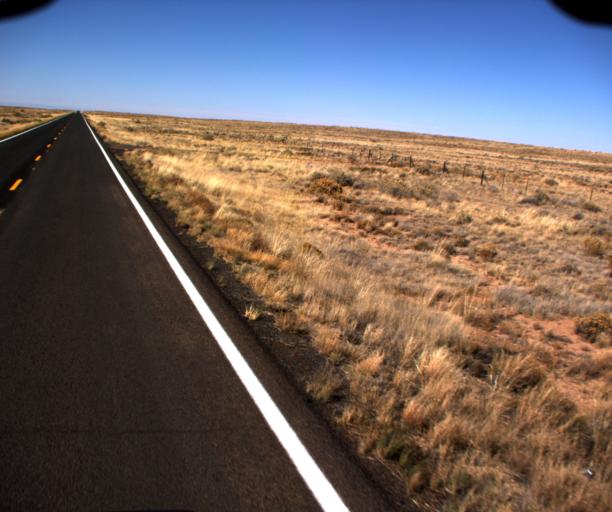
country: US
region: Arizona
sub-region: Coconino County
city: Tuba City
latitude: 35.9631
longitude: -110.9445
